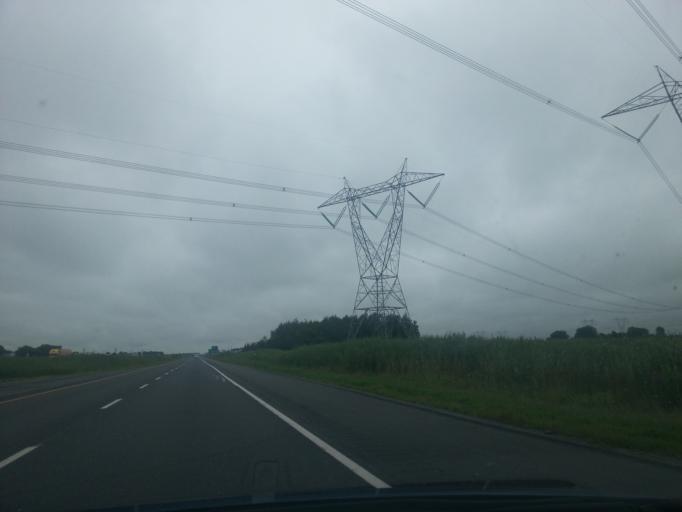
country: CA
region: Quebec
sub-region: Mauricie
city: Saint-Cyrille-de-Wendover
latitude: 45.9234
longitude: -72.4715
